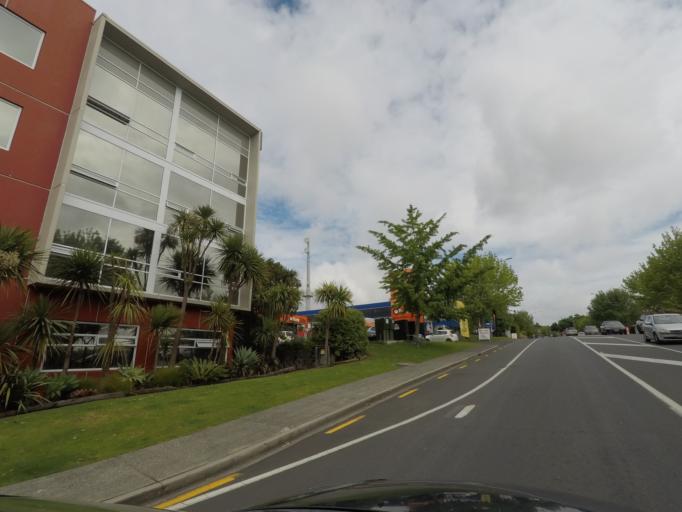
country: NZ
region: Auckland
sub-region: Auckland
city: Rosebank
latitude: -36.8752
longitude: 174.6308
